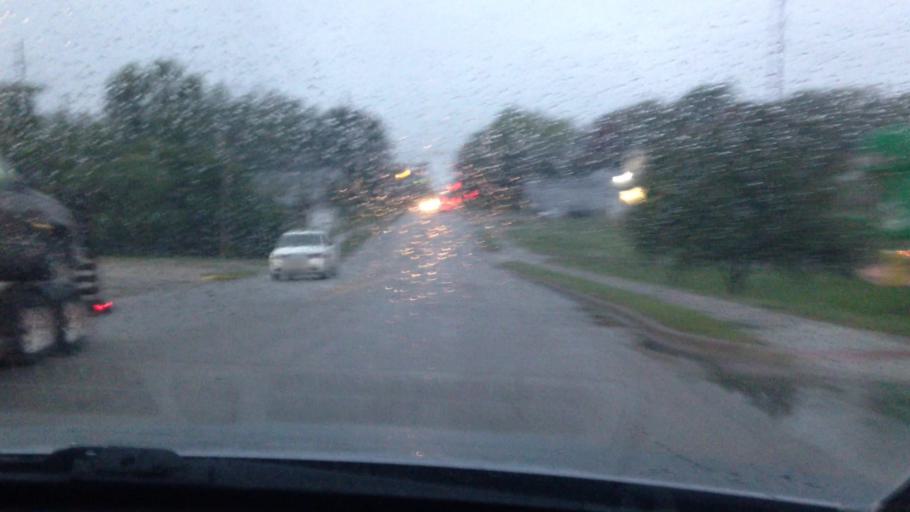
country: US
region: Kansas
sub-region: Leavenworth County
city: Leavenworth
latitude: 39.3104
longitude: -94.9245
